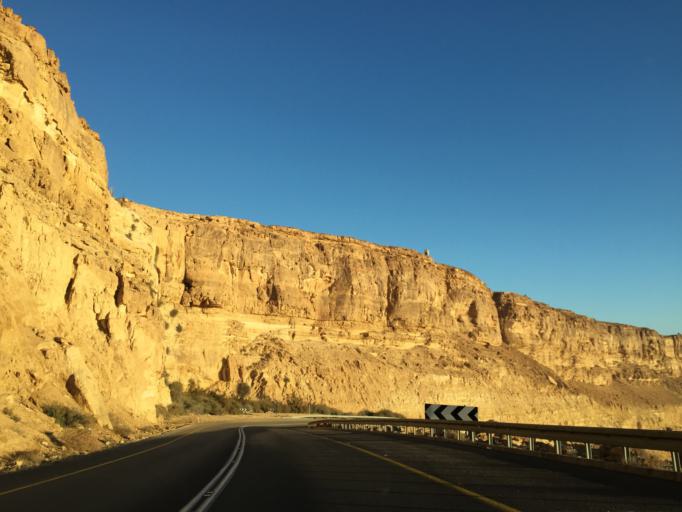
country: IL
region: Southern District
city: Mitzpe Ramon
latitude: 30.6153
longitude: 34.8092
